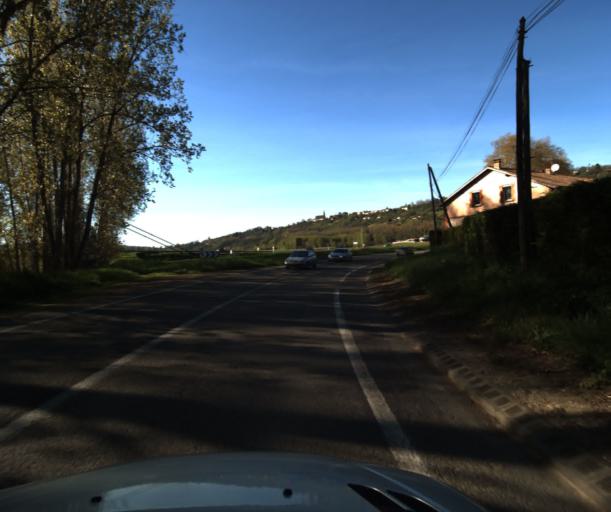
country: FR
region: Midi-Pyrenees
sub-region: Departement du Tarn-et-Garonne
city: Lafrancaise
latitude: 44.1138
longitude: 1.2490
